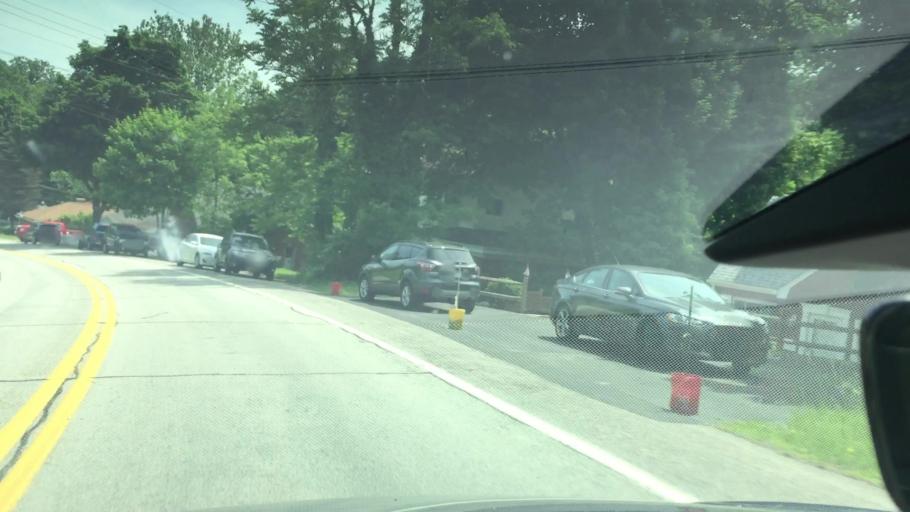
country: US
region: Pennsylvania
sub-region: Allegheny County
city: Penn Hills
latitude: 40.4799
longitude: -79.8340
